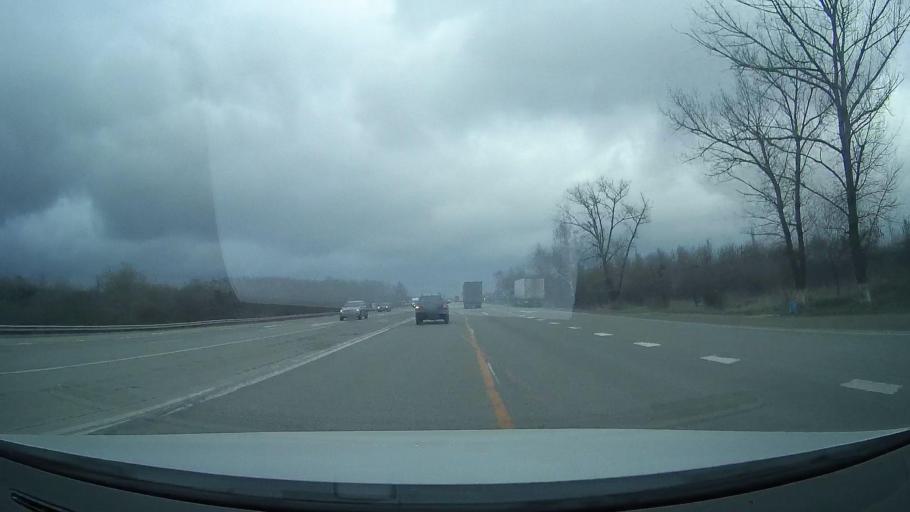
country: RU
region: Rostov
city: Grushevskaya
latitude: 47.5317
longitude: 39.9696
